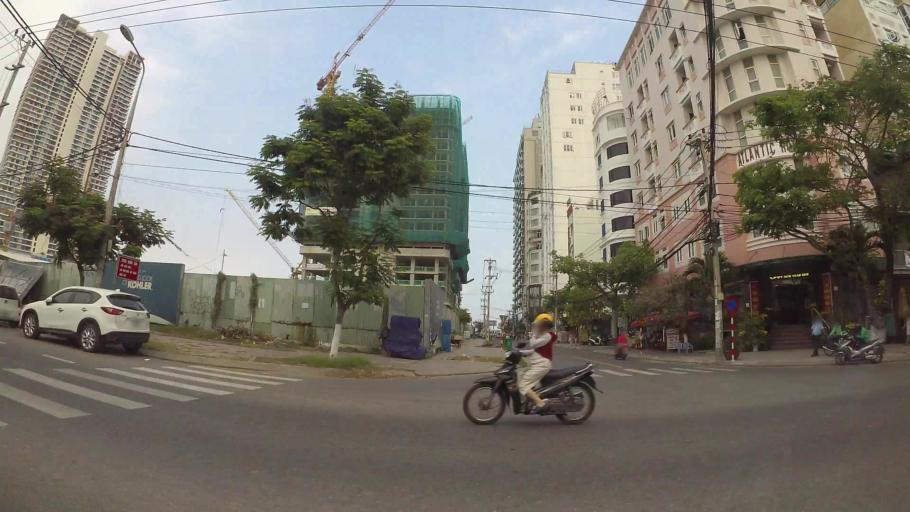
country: VN
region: Da Nang
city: Son Tra
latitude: 16.0689
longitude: 108.2430
